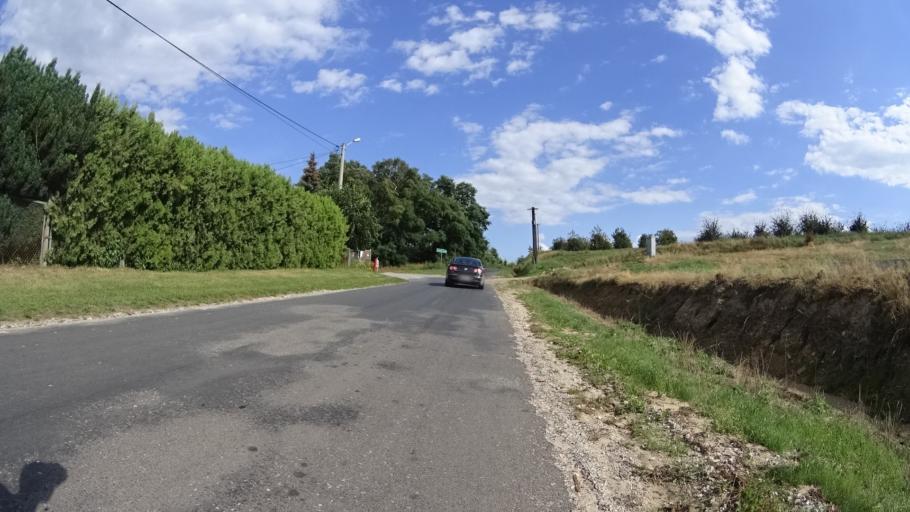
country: PL
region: Masovian Voivodeship
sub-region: Powiat grojecki
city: Mogielnica
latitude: 51.6901
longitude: 20.7470
